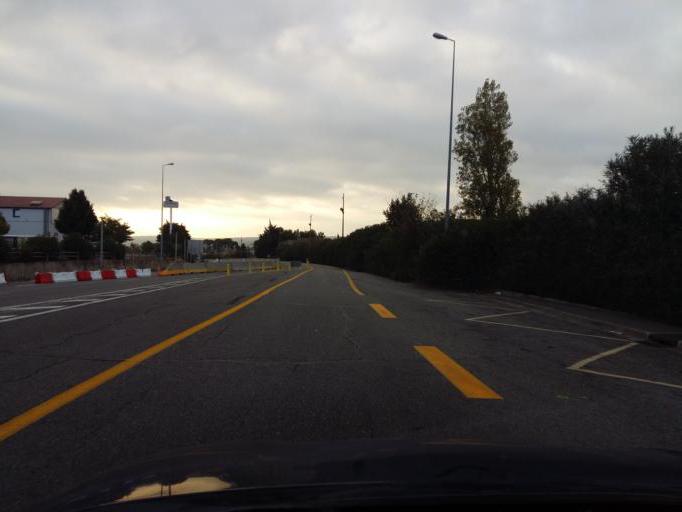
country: FR
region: Provence-Alpes-Cote d'Azur
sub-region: Departement des Bouches-du-Rhone
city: Martigues
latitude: 43.4293
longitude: 5.0477
